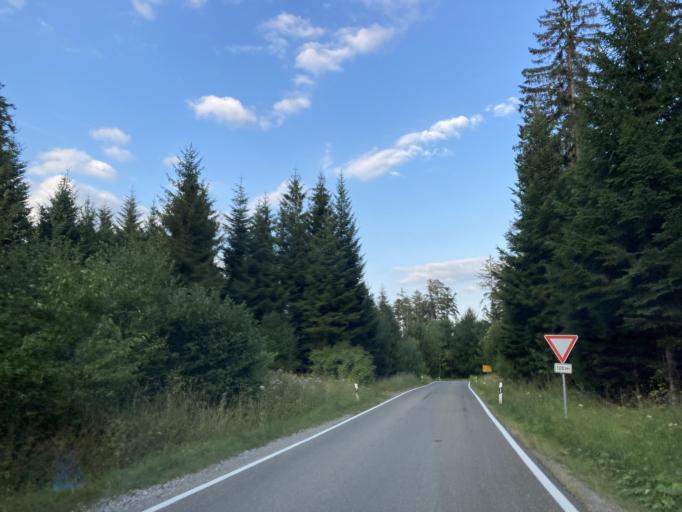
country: DE
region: Baden-Wuerttemberg
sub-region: Karlsruhe Region
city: Neubulach
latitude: 48.6422
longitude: 8.6659
